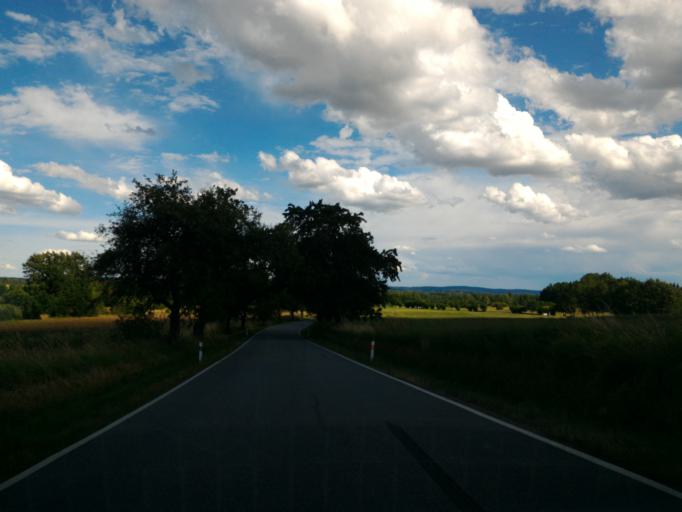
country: CZ
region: Vysocina
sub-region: Okres Jihlava
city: Telc
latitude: 49.2163
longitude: 15.4262
